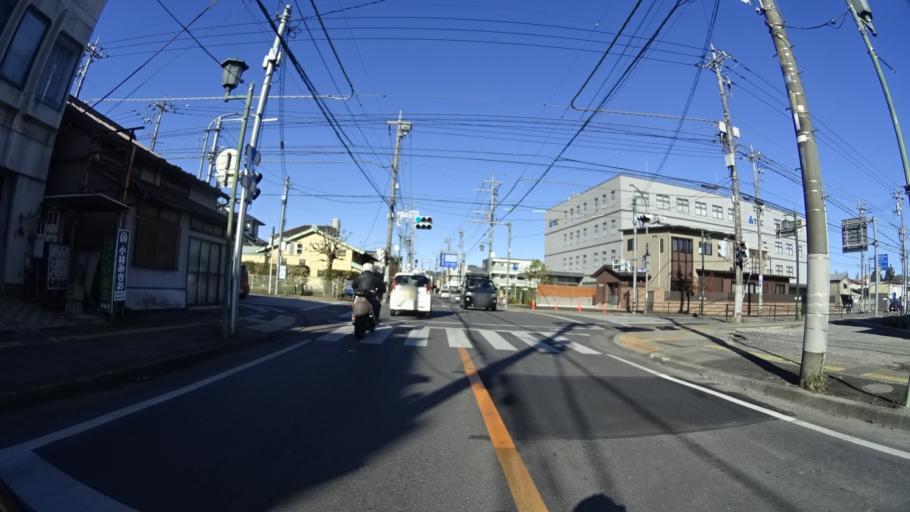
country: JP
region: Tochigi
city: Kanuma
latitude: 36.5670
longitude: 139.7472
